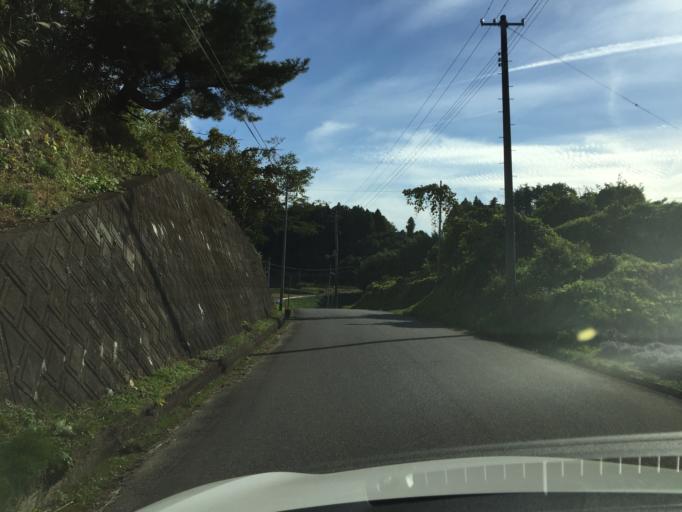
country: JP
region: Fukushima
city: Miharu
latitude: 37.3454
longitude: 140.4963
